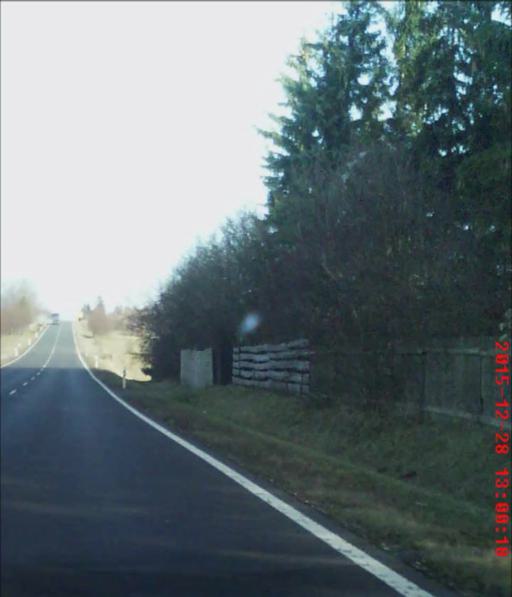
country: DE
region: Thuringia
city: Niederrossla
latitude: 51.0264
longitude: 11.4906
